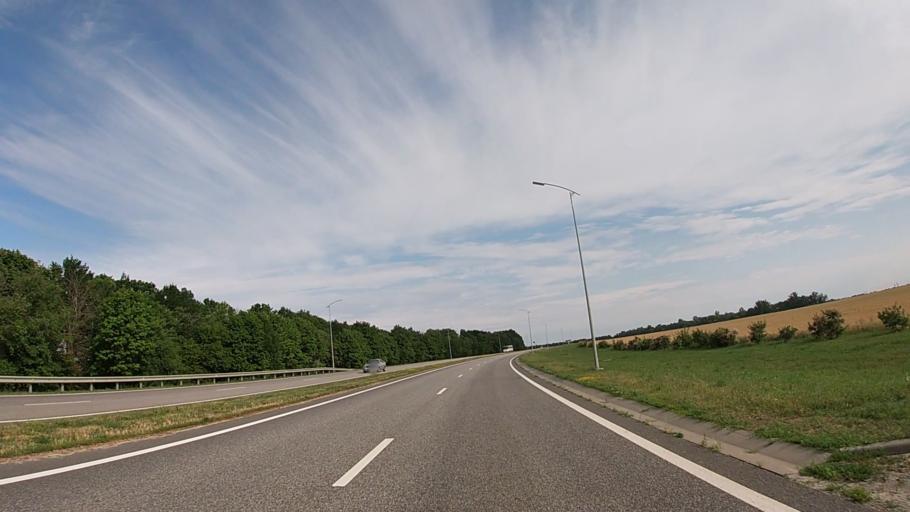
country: RU
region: Belgorod
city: Borisovka
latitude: 50.7555
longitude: 35.9661
